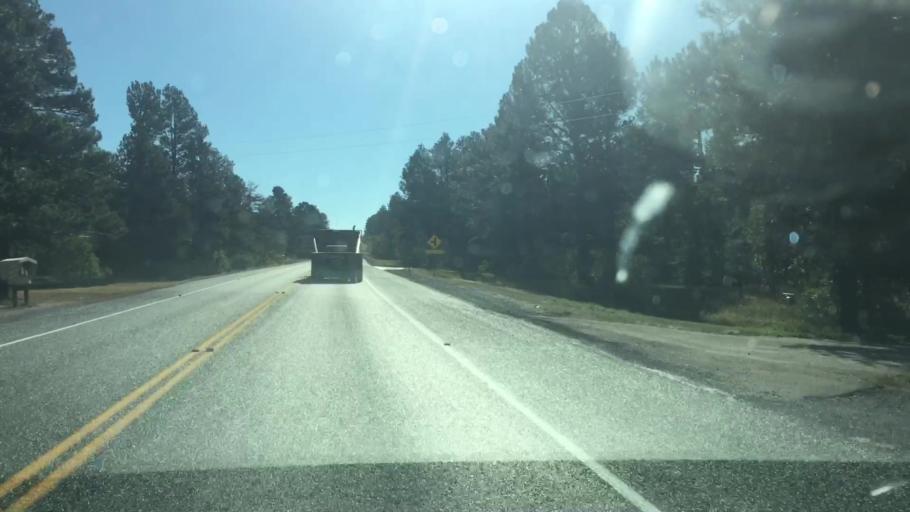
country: US
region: Colorado
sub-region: Douglas County
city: The Pinery
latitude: 39.3873
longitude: -104.7369
